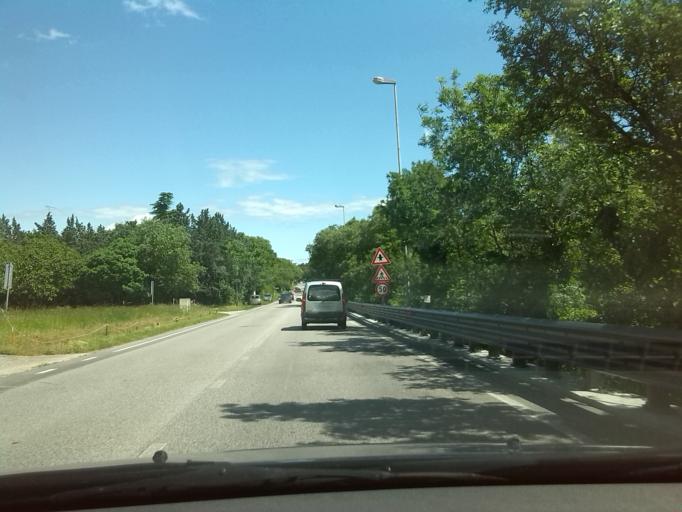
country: IT
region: Friuli Venezia Giulia
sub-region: Provincia di Trieste
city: Duino
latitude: 45.7766
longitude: 13.6023
